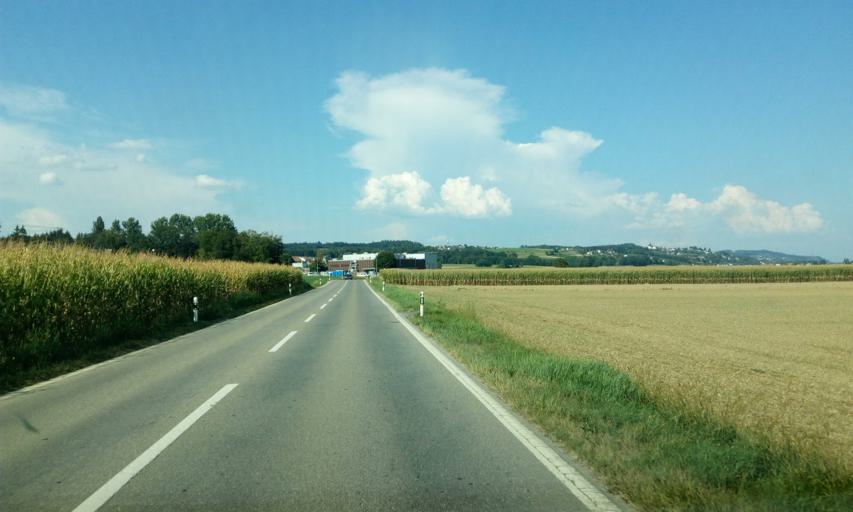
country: CH
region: Fribourg
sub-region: Broye District
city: Domdidier
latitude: 46.8978
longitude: 6.9906
